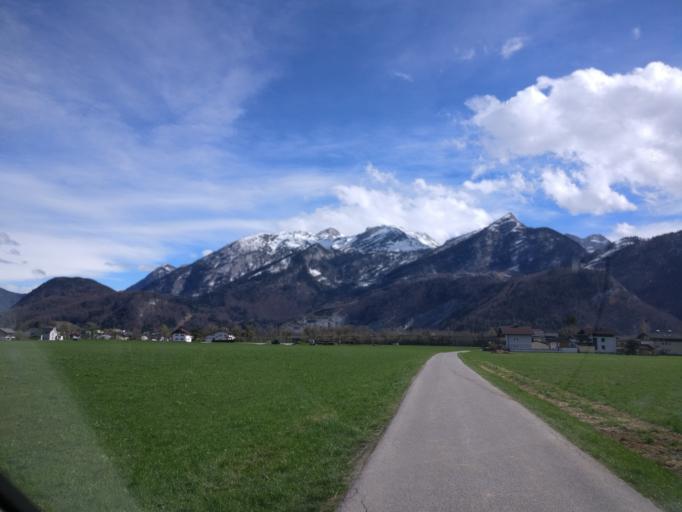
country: AT
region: Salzburg
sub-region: Politischer Bezirk Hallein
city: Golling an der Salzach
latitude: 47.5955
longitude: 13.1566
